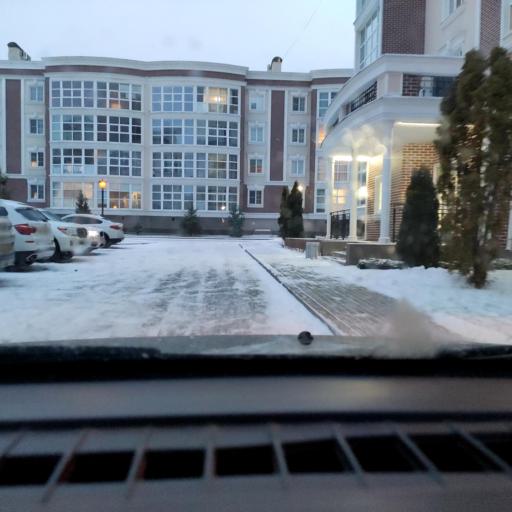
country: RU
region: Samara
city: Tol'yatti
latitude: 53.4965
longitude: 49.2936
